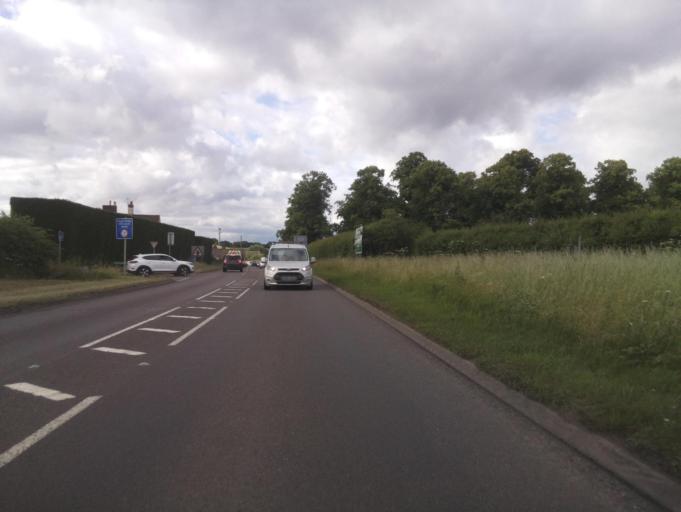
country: GB
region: England
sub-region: Worcestershire
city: Kidderminster
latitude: 52.4403
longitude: -2.2116
